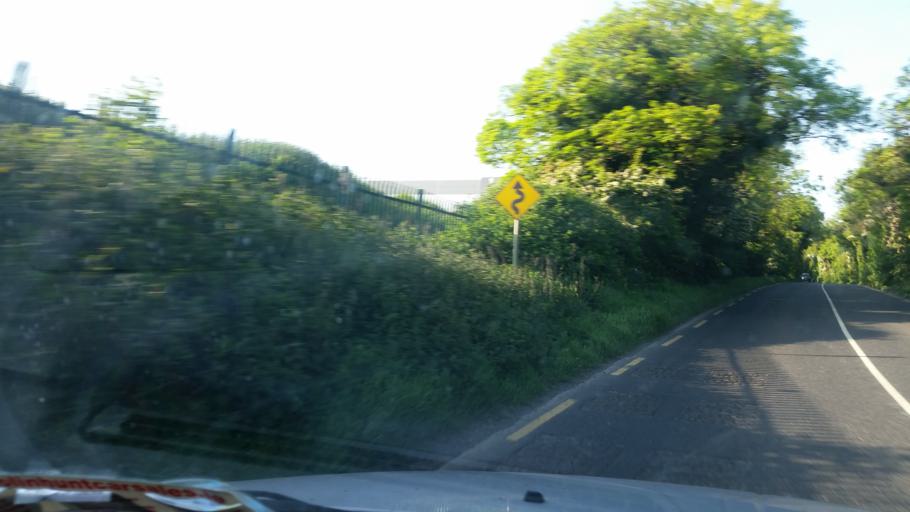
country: IE
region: Leinster
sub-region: Fingal County
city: Blanchardstown
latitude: 53.4188
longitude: -6.3423
